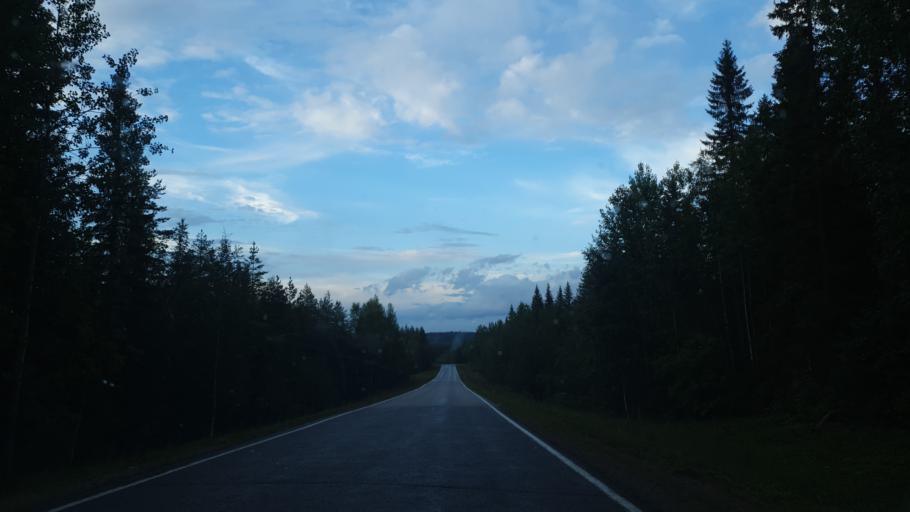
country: FI
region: North Karelia
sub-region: Pielisen Karjala
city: Lieksa
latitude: 63.7530
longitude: 29.8555
